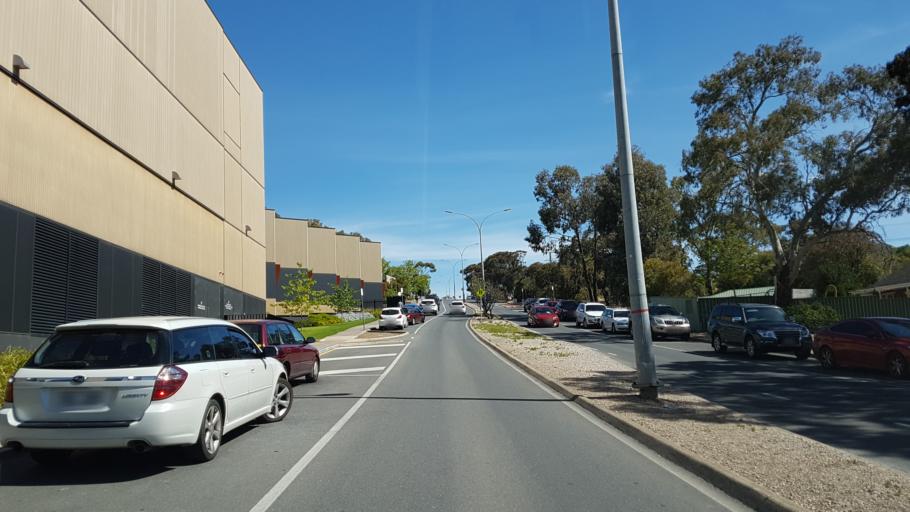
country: AU
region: South Australia
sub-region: Marion
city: Marion
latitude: -35.0234
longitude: 138.5679
